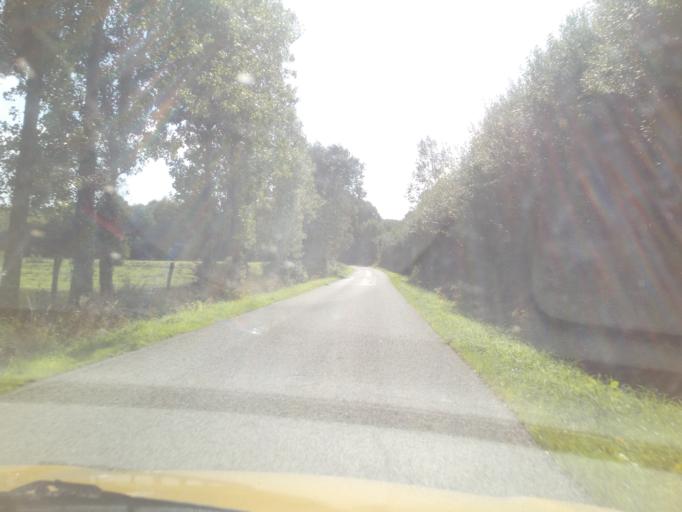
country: FR
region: Brittany
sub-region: Departement des Cotes-d'Armor
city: Merdrignac
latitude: 48.1728
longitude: -2.4187
